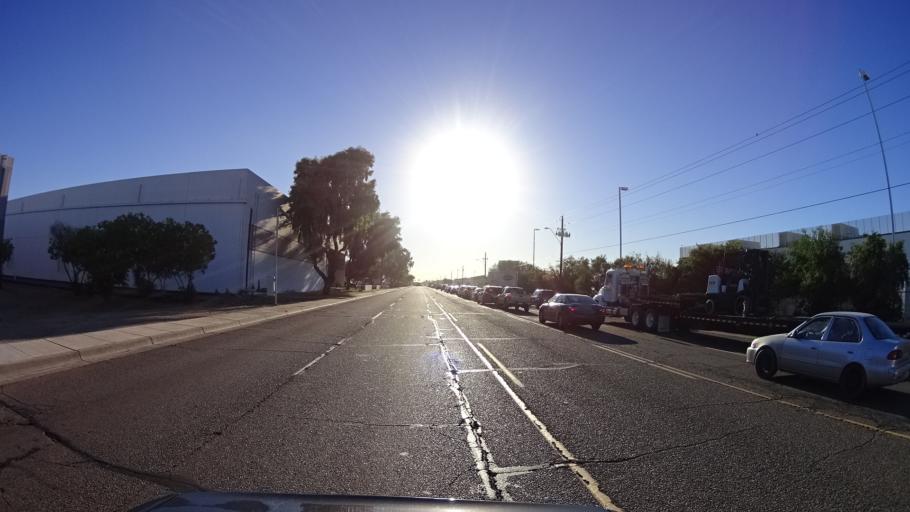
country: US
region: Arizona
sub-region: Maricopa County
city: Laveen
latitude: 33.4369
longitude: -112.1736
